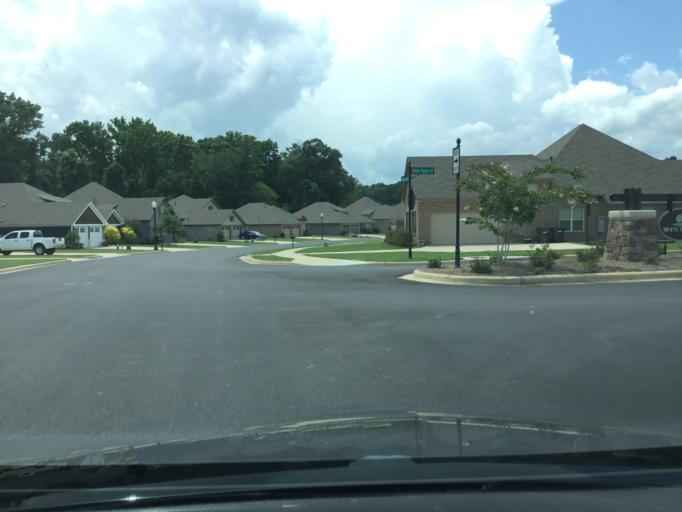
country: US
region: Alabama
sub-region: Montgomery County
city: Pike Road
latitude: 32.3361
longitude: -86.0784
